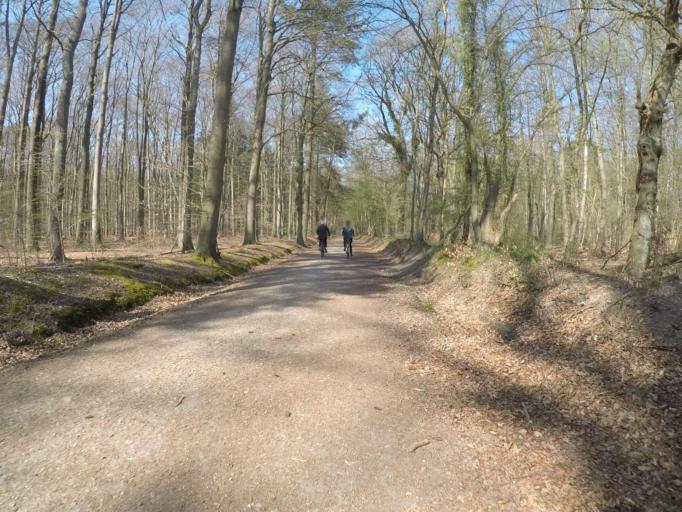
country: DE
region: Schleswig-Holstein
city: Rellingen
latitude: 53.6122
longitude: 9.7831
